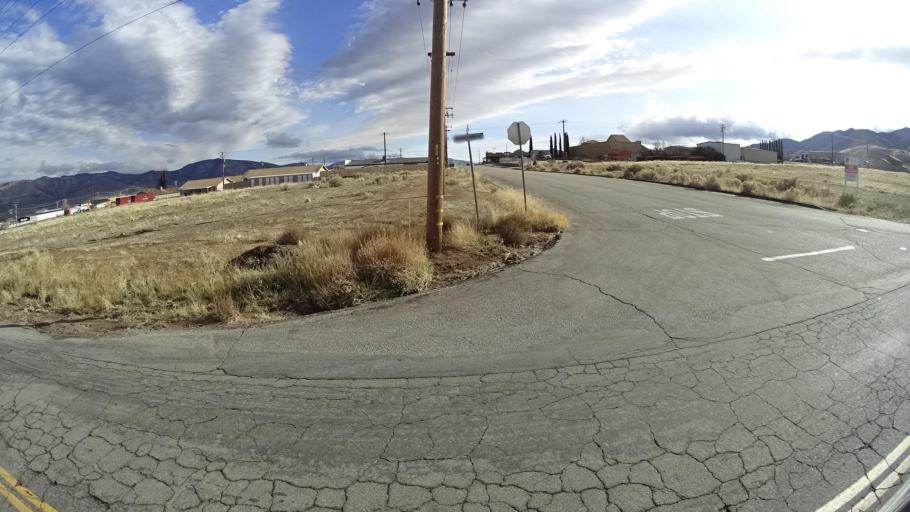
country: US
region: California
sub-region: Kern County
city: Golden Hills
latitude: 35.1207
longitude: -118.4950
